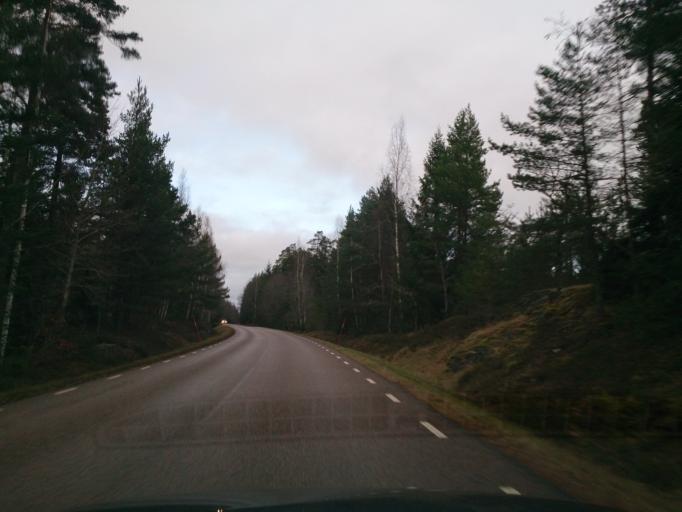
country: SE
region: OEstergoetland
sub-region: Atvidabergs Kommun
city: Atvidaberg
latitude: 58.2504
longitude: 16.0182
